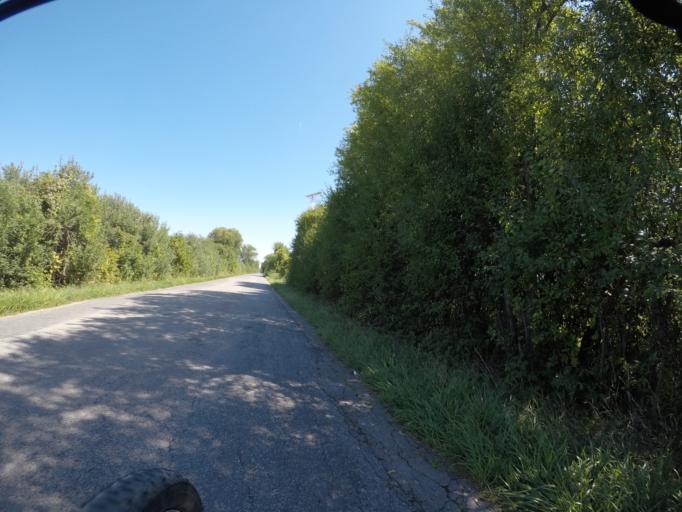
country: AT
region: Lower Austria
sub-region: Politischer Bezirk Wien-Umgebung
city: Moosbrunn
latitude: 48.0053
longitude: 16.4572
